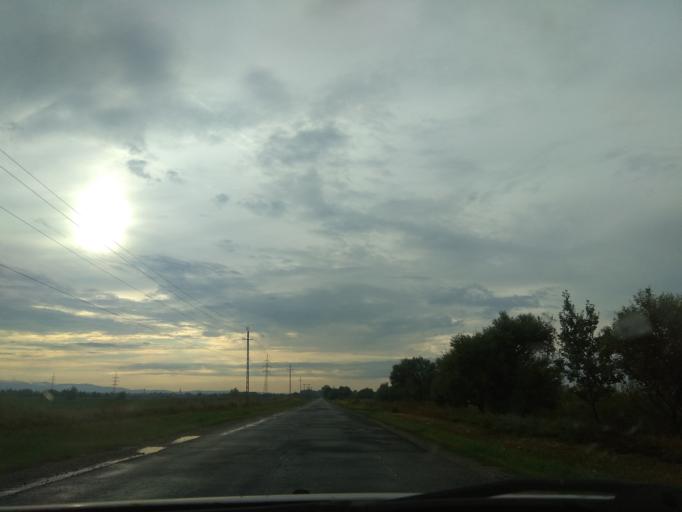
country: HU
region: Borsod-Abauj-Zemplen
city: Onga
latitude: 48.1147
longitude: 20.9417
